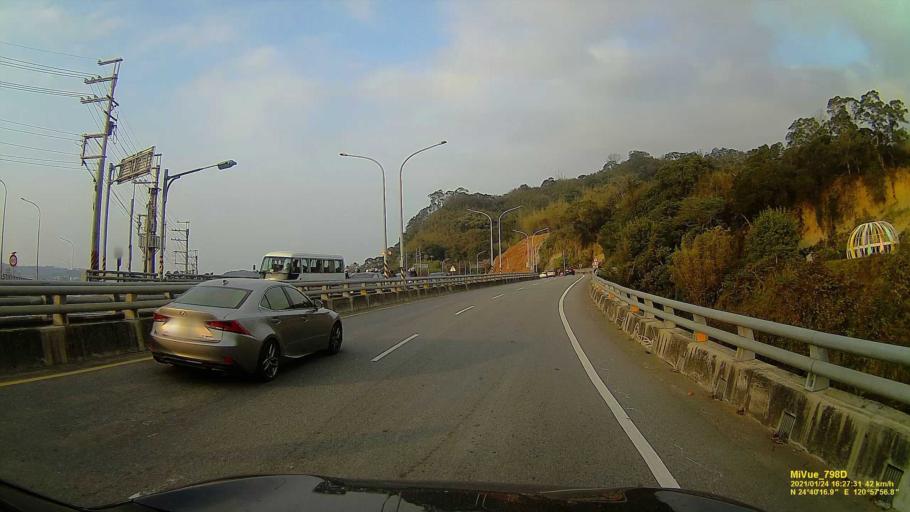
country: TW
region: Taiwan
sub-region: Hsinchu
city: Hsinchu
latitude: 24.6717
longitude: 120.9658
